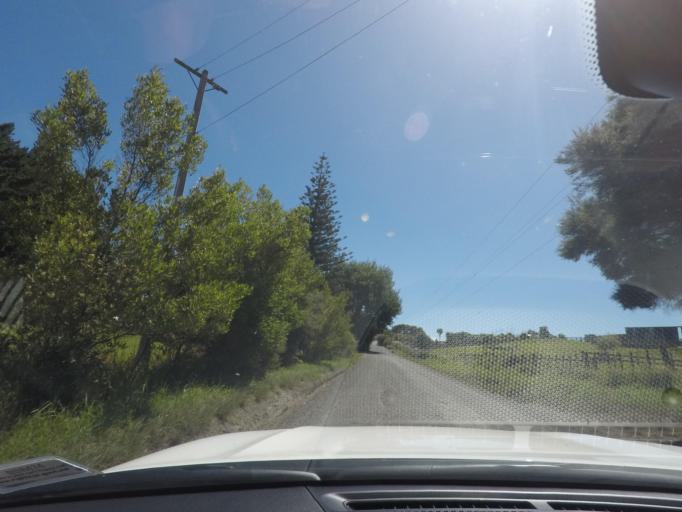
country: NZ
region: Auckland
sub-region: Auckland
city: Parakai
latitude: -36.5809
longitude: 174.3170
